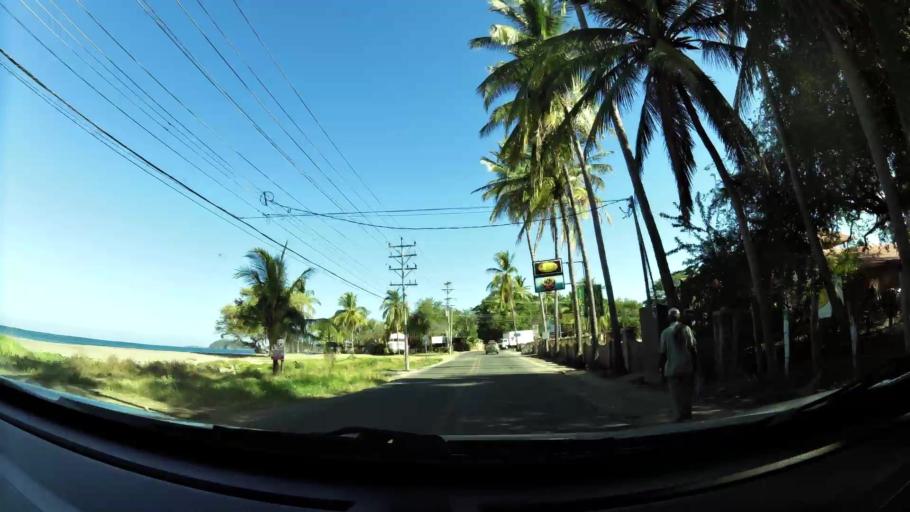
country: CR
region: Guanacaste
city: Sardinal
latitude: 10.4085
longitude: -85.7967
